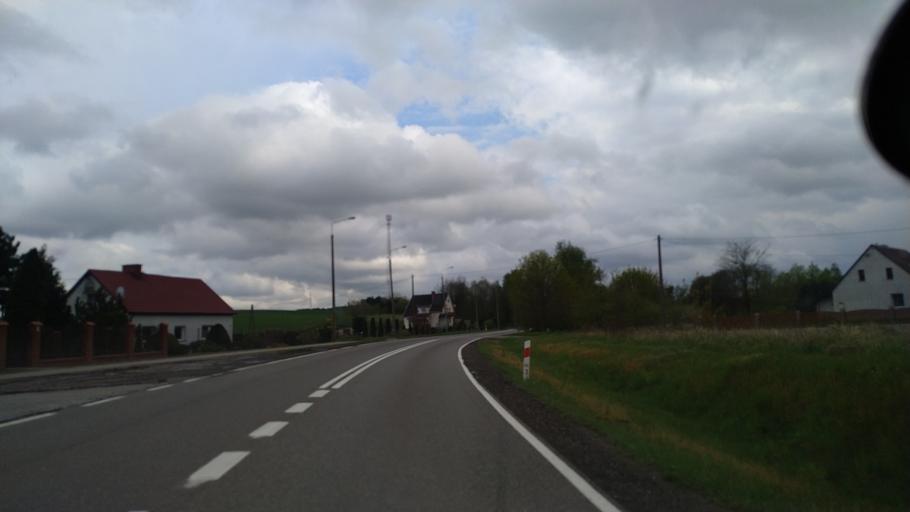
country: PL
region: Pomeranian Voivodeship
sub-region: Powiat kwidzynski
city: Ryjewo
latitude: 53.8015
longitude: 18.9638
